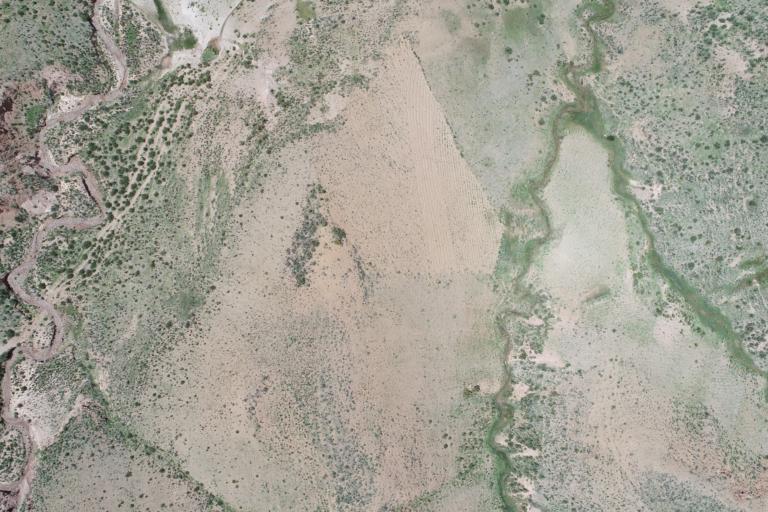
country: BO
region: La Paz
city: Curahuara de Carangas
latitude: -17.3238
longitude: -68.5121
